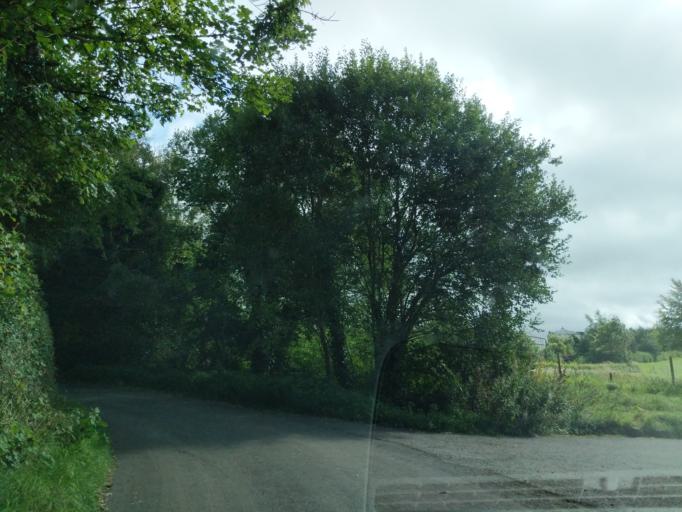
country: GB
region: Scotland
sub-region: The Scottish Borders
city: Kelso
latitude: 55.5665
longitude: -2.4727
